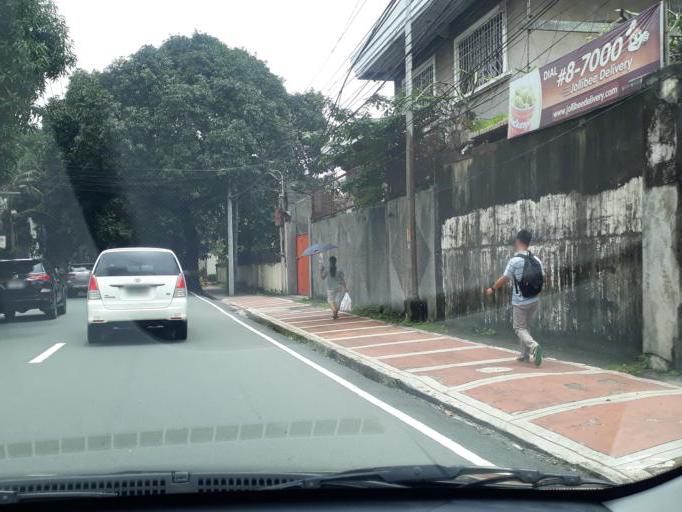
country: PH
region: Metro Manila
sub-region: San Juan
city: San Juan
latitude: 14.6216
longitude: 121.0299
